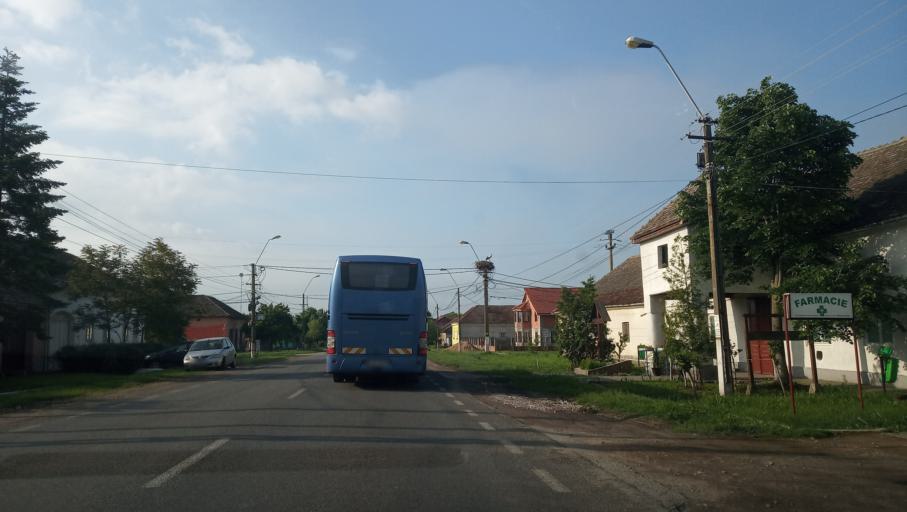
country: RO
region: Timis
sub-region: Comuna Moravita
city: Moravita
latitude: 45.2601
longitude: 21.2659
